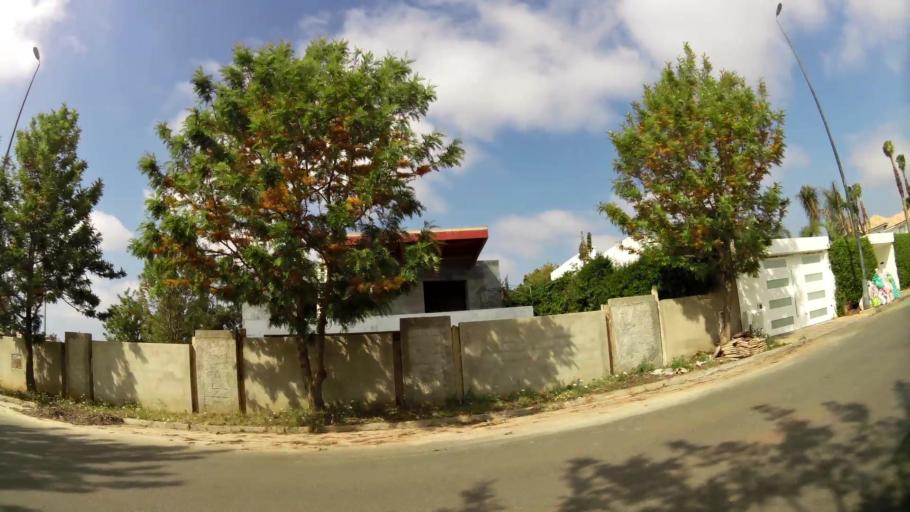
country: MA
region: Rabat-Sale-Zemmour-Zaer
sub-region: Rabat
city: Rabat
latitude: 33.9729
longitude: -6.8484
